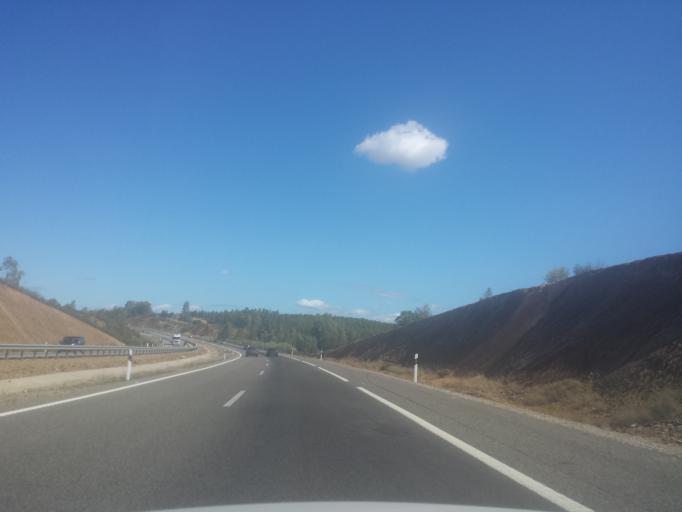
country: ES
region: Andalusia
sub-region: Provincia de Sevilla
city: El Ronquillo
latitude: 37.8095
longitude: -6.2035
